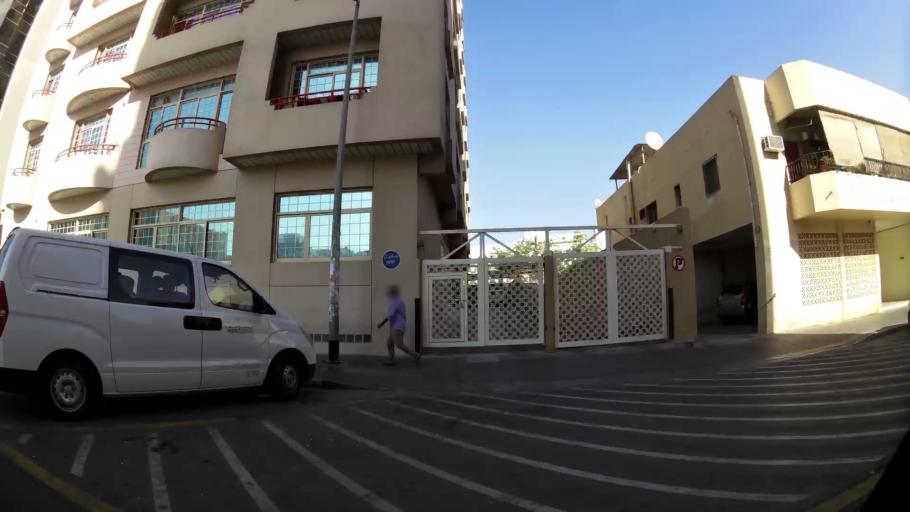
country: AE
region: Ash Shariqah
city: Sharjah
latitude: 25.2579
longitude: 55.2903
